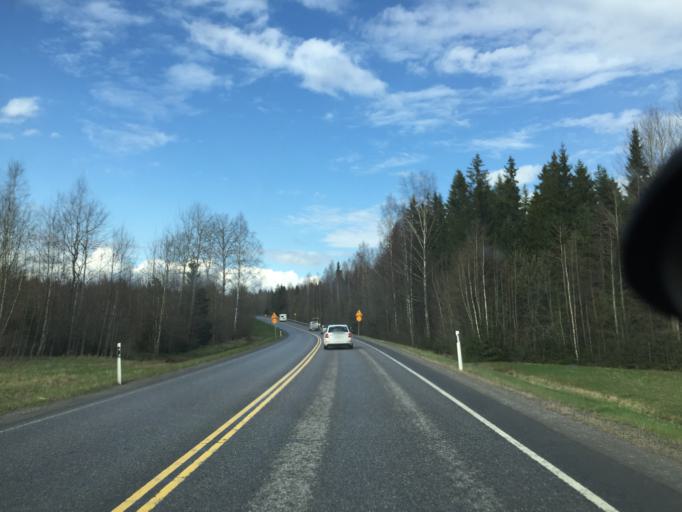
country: FI
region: Uusimaa
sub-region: Helsinki
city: Lohja
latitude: 60.2105
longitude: 24.0265
